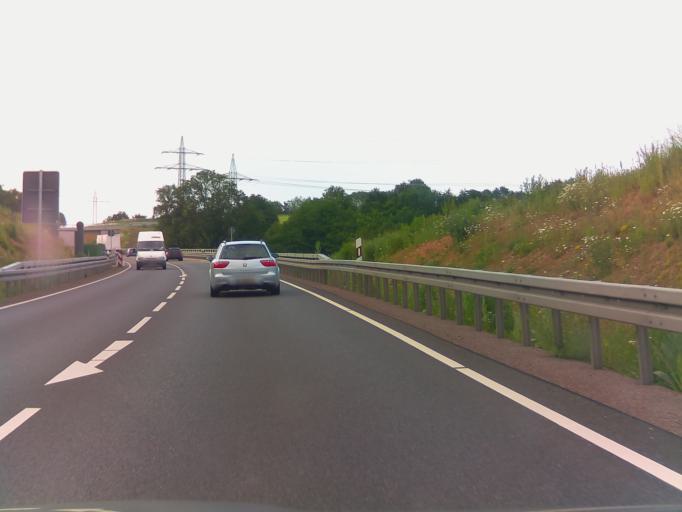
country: DE
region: Hesse
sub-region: Regierungsbezirk Kassel
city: Bad Hersfeld
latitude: 50.8344
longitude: 9.7290
